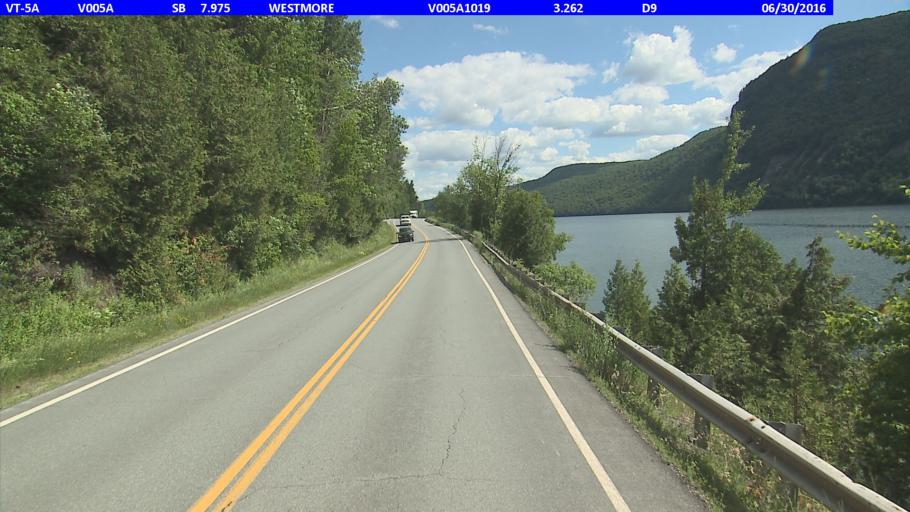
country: US
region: Vermont
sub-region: Caledonia County
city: Lyndonville
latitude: 44.7382
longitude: -72.0460
